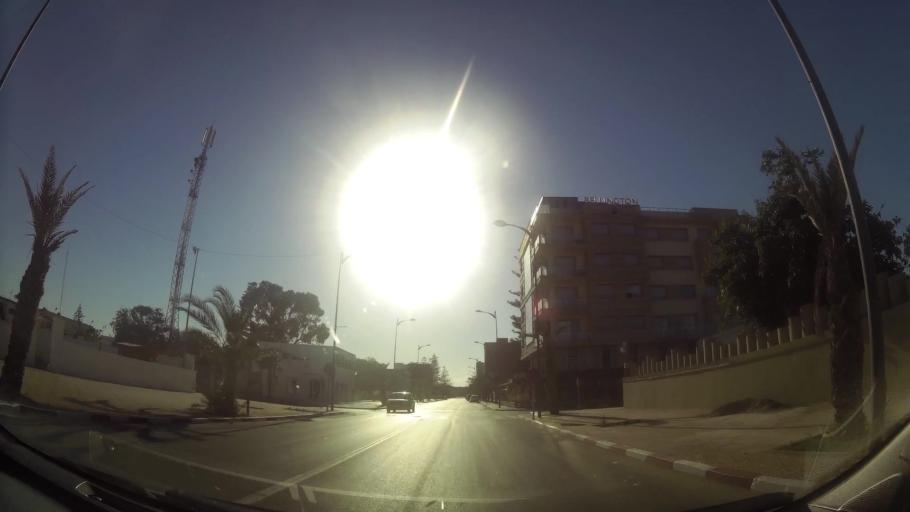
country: MA
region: Oriental
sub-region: Berkane-Taourirt
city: Madagh
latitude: 35.0859
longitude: -2.2258
